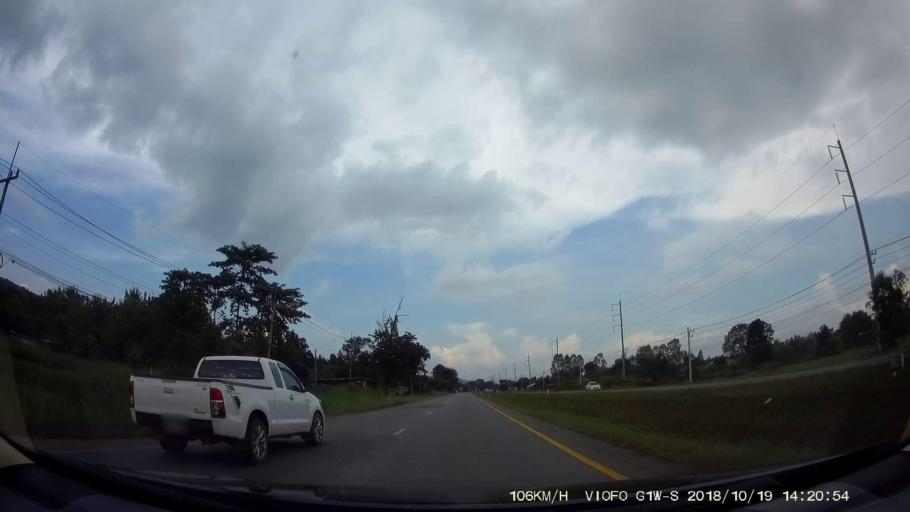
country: TH
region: Chaiyaphum
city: Kaeng Khro
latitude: 16.0460
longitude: 102.2605
